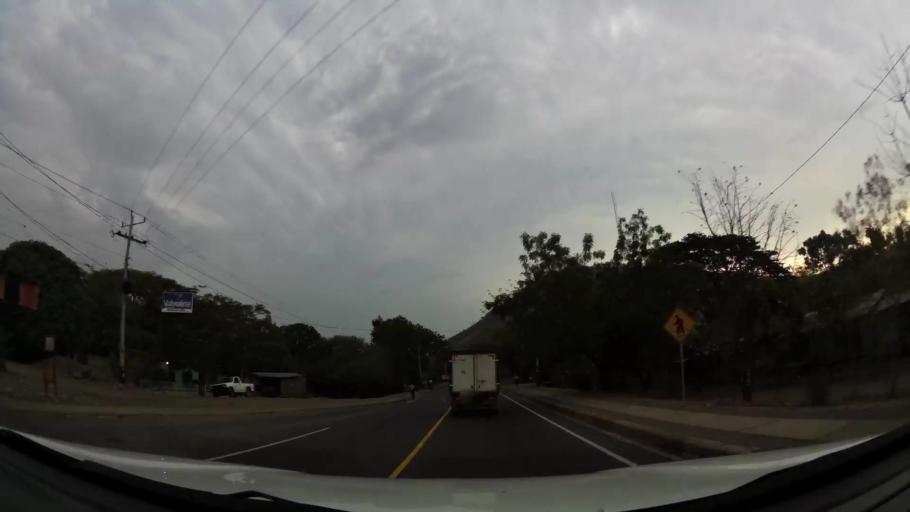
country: NI
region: Matagalpa
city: Ciudad Dario
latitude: 12.9303
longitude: -86.1978
